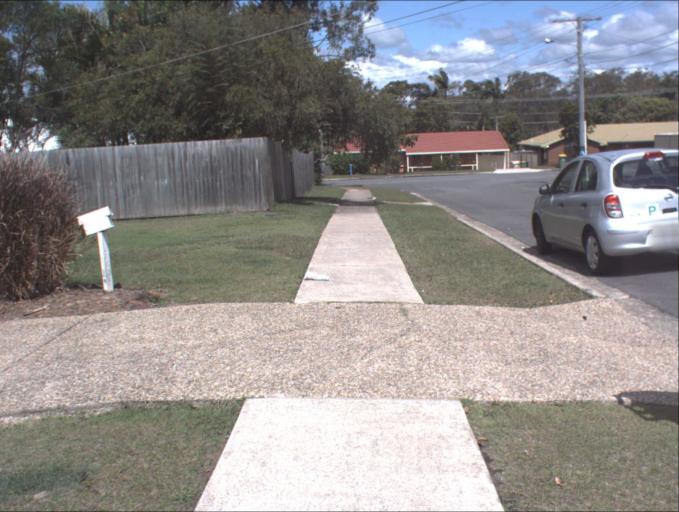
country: AU
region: Queensland
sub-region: Logan
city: Park Ridge South
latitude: -27.6669
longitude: 153.0258
